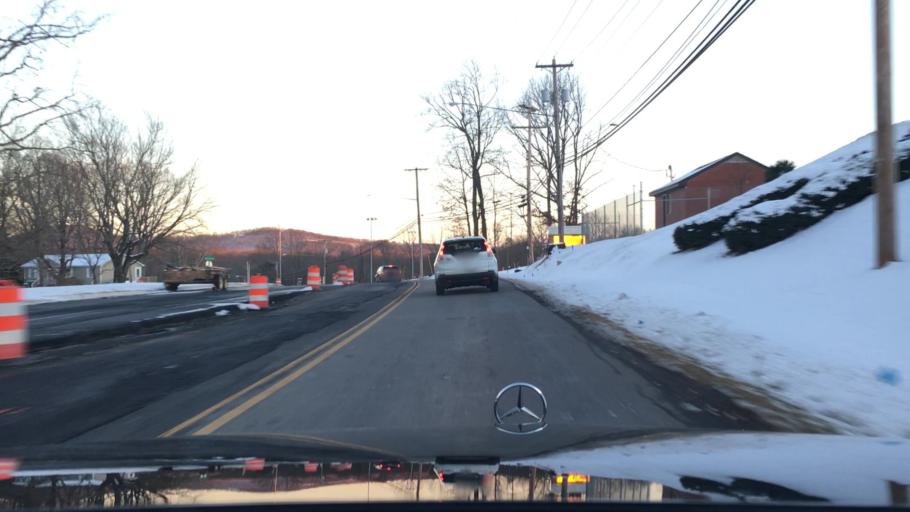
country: US
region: Virginia
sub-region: City of Lynchburg
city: West Lynchburg
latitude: 37.3633
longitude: -79.2045
